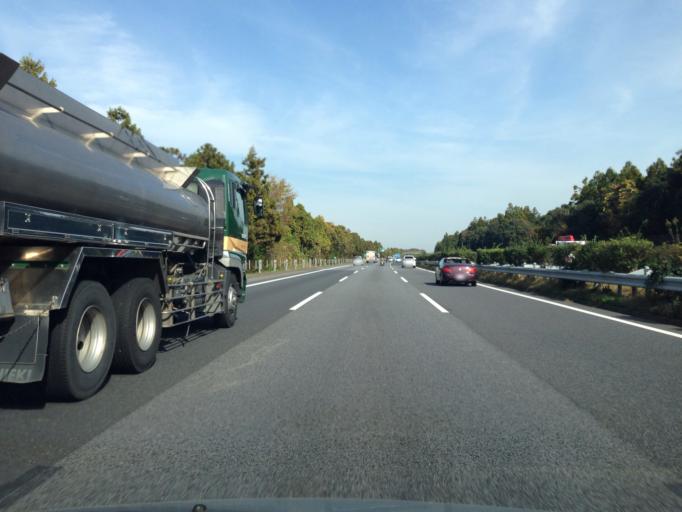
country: JP
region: Ibaraki
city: Naka
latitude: 36.1292
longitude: 140.1926
